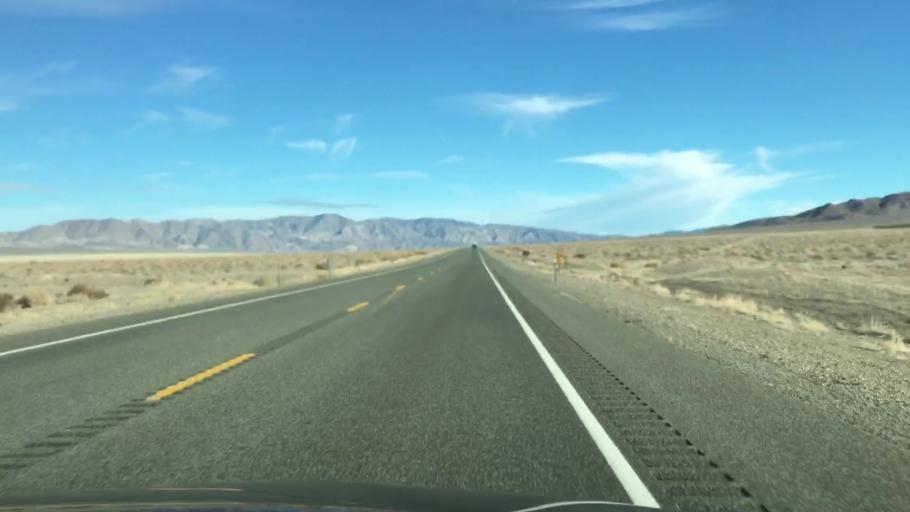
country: US
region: Nevada
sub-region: Mineral County
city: Hawthorne
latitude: 38.5370
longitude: -118.3354
